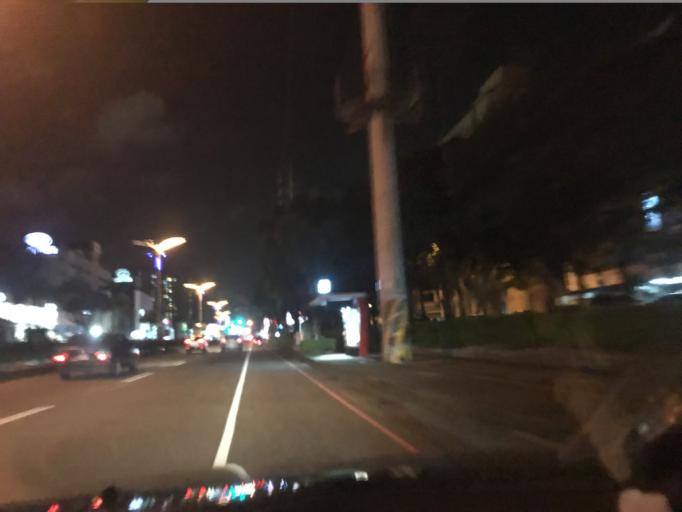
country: TW
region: Taiwan
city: Taoyuan City
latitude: 24.9714
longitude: 121.2361
